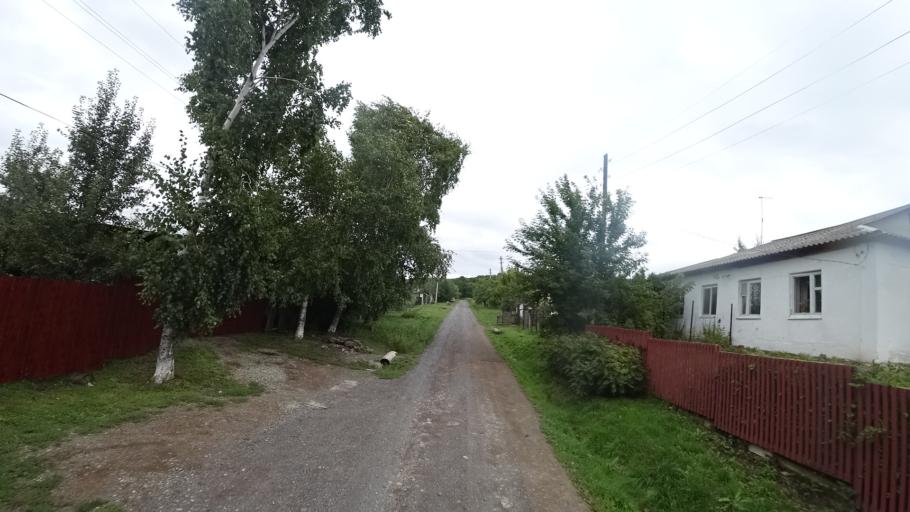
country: RU
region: Primorskiy
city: Chernigovka
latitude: 44.4572
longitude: 132.5952
